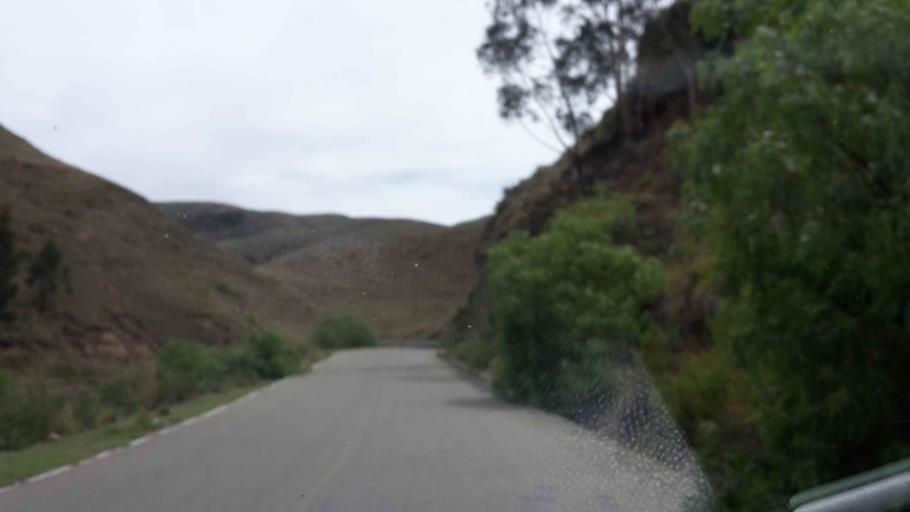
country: BO
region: Cochabamba
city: Colomi
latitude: -17.4000
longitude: -65.8056
